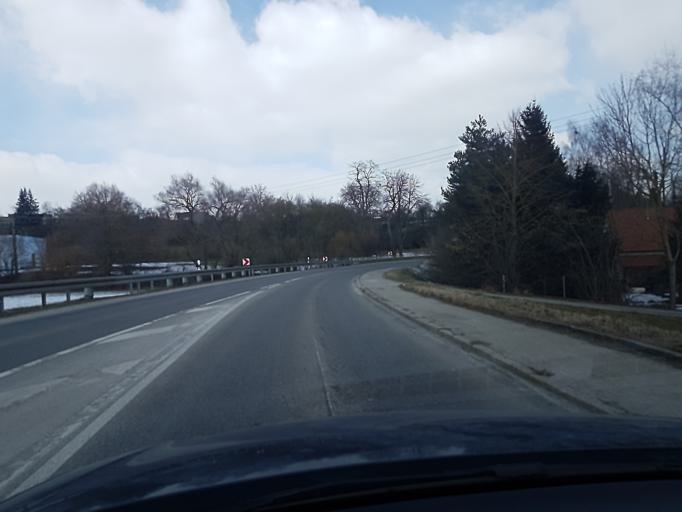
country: DE
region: Baden-Wuerttemberg
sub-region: Regierungsbezirk Stuttgart
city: Herrenberg
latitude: 48.5840
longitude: 8.8618
